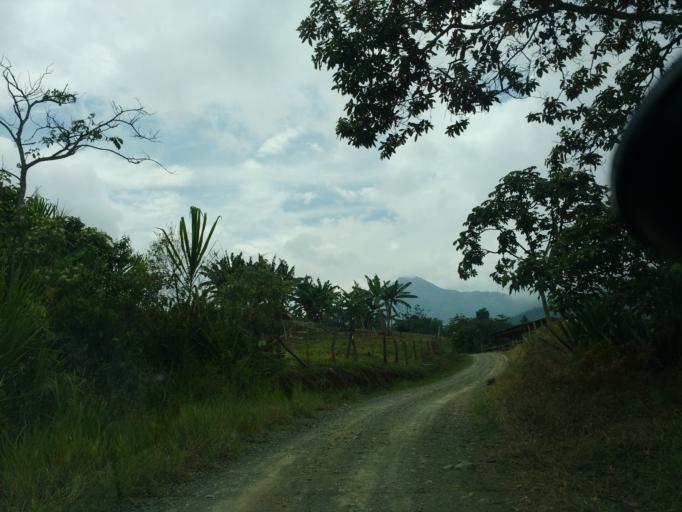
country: CO
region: Cauca
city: Santander de Quilichao
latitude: 2.9148
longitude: -76.4793
